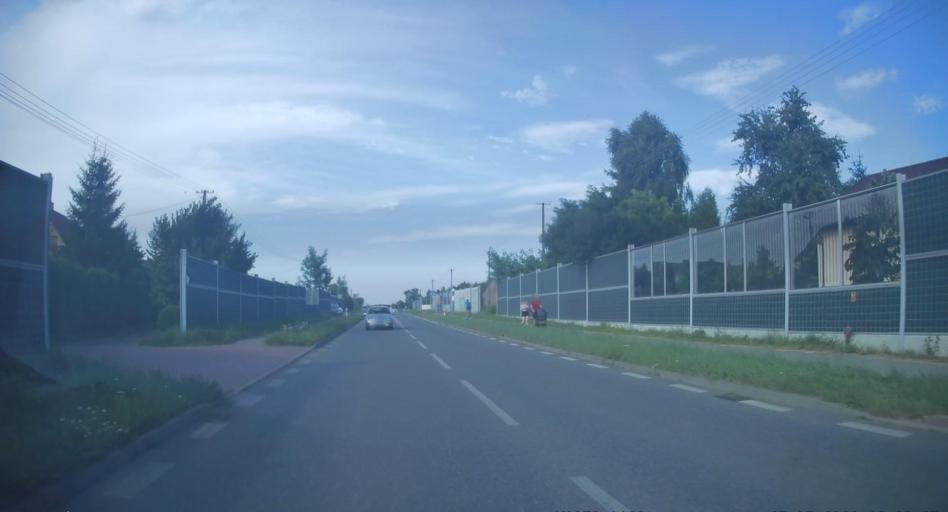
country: PL
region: Swietokrzyskie
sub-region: Powiat konecki
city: Konskie
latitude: 51.1667
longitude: 20.3774
